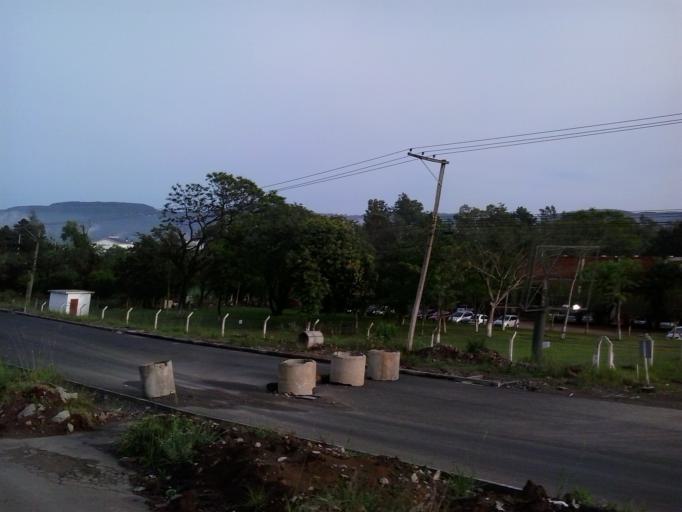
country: BR
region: Rio Grande do Sul
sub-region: Santa Maria
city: Santa Maria
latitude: -29.6972
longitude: -53.7343
